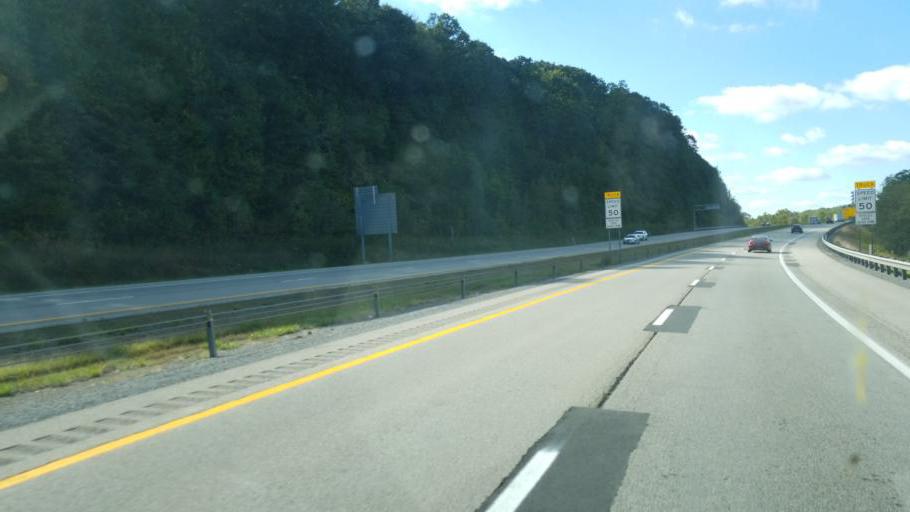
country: US
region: West Virginia
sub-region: Monongalia County
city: Cheat Lake
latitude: 39.6589
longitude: -79.7922
